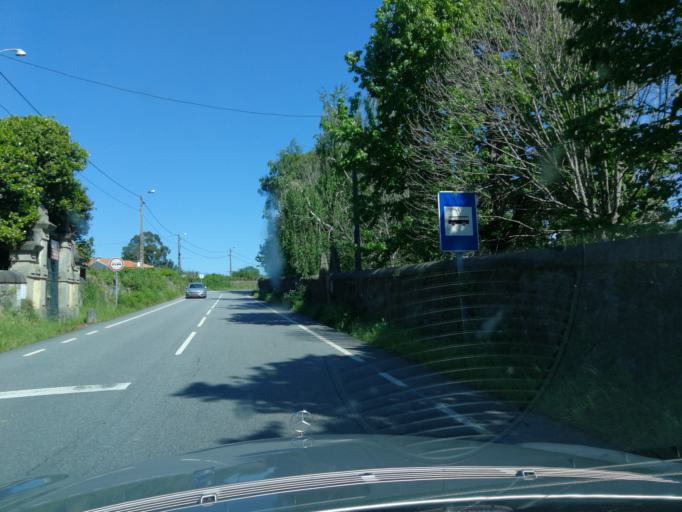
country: PT
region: Viana do Castelo
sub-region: Viana do Castelo
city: Darque
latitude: 41.7113
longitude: -8.7515
